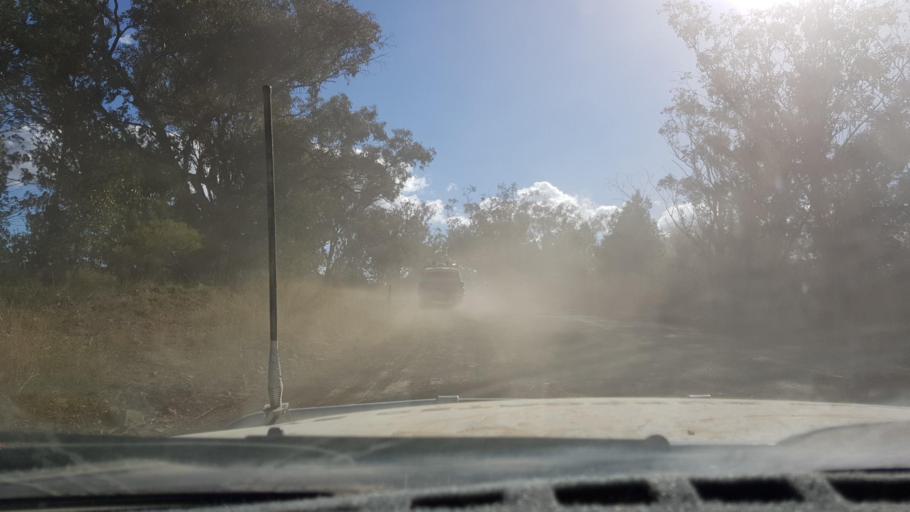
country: AU
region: New South Wales
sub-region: Tamworth Municipality
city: Manilla
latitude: -30.6524
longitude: 150.4938
